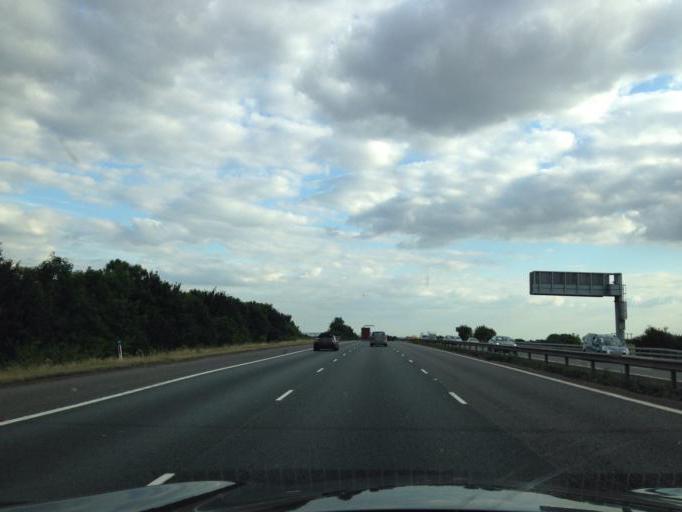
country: GB
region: England
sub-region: Oxfordshire
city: Bicester
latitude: 51.9306
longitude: -1.2018
